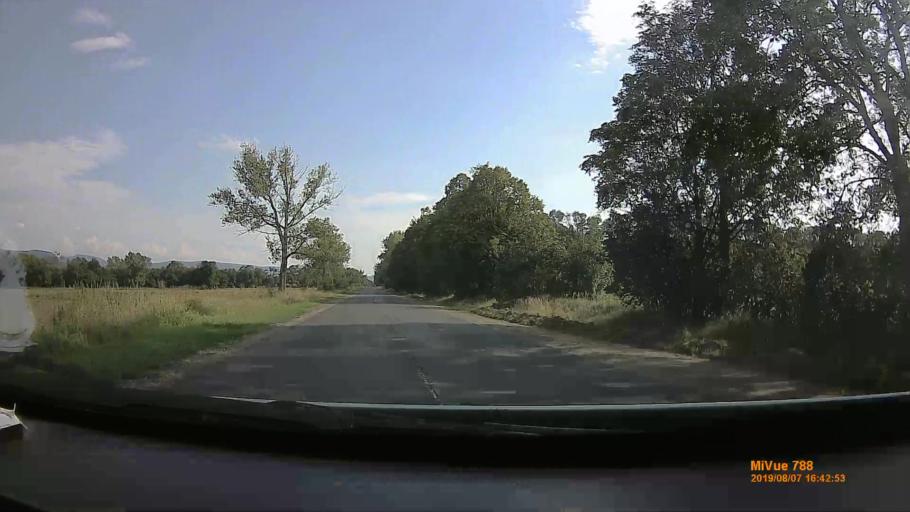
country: HU
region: Borsod-Abauj-Zemplen
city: Abaujszanto
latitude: 48.3648
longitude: 21.2158
